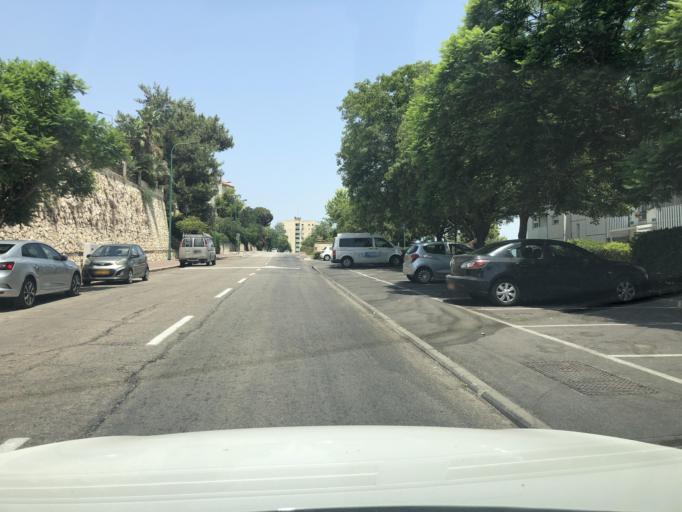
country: IL
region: Haifa
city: Daliyat el Karmil
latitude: 32.6506
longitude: 35.0964
